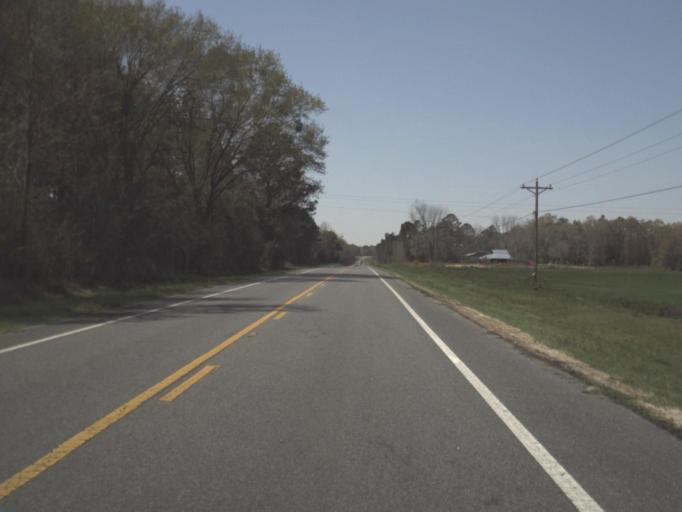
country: US
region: Alabama
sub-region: Geneva County
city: Geneva
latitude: 30.9573
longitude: -85.9022
